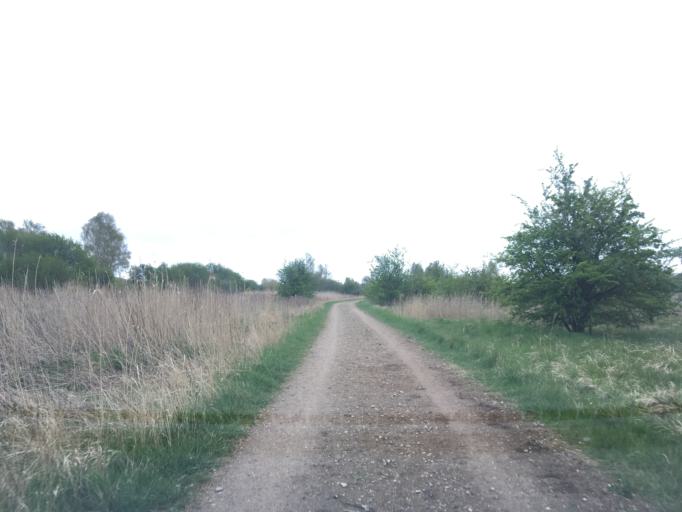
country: DK
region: Capital Region
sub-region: Tarnby Kommune
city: Tarnby
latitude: 55.5901
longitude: 12.5703
